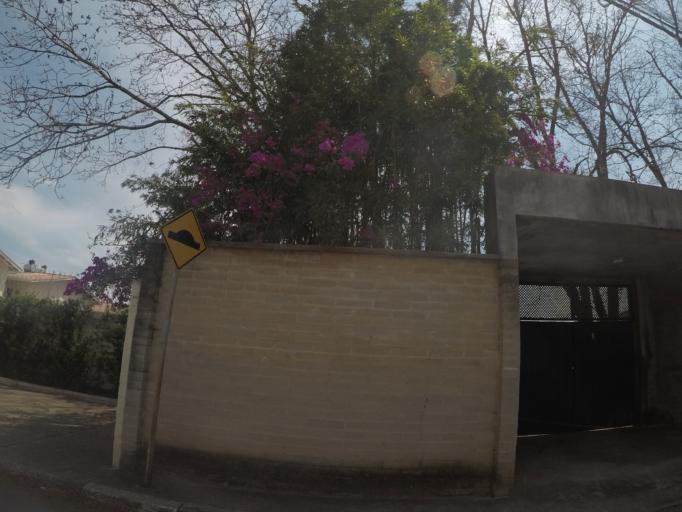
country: BR
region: Sao Paulo
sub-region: Cabreuva
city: Cabreuva
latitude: -23.2462
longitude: -47.0628
